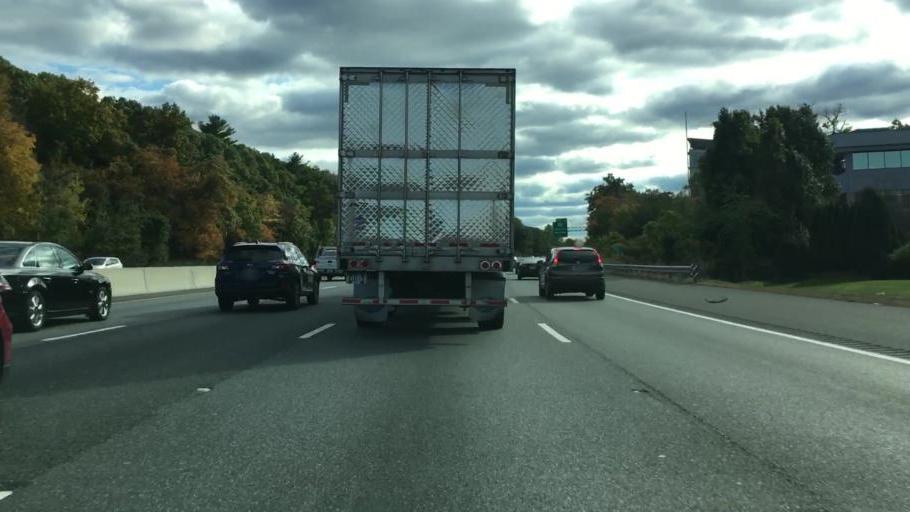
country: US
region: Massachusetts
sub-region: Middlesex County
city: Waltham
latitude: 42.3881
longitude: -71.2621
